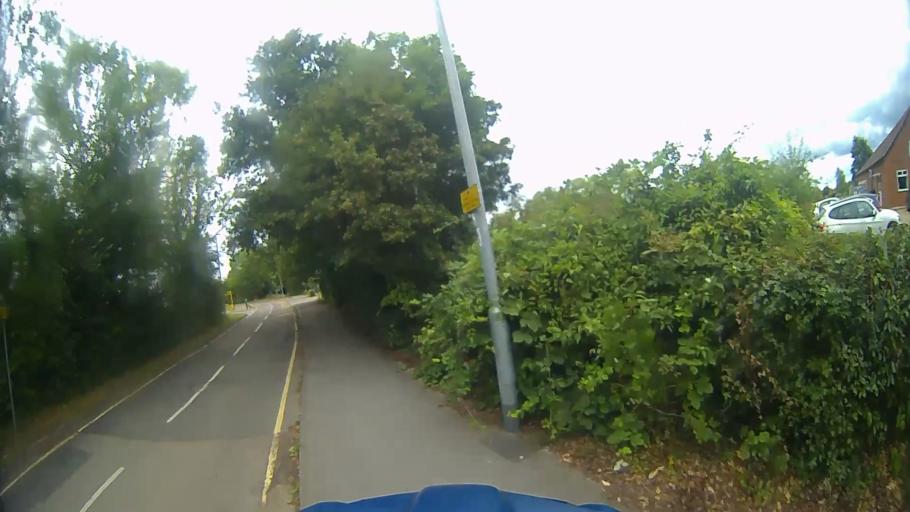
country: GB
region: England
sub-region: Wokingham
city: Winnersh
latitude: 51.4270
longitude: -0.8679
